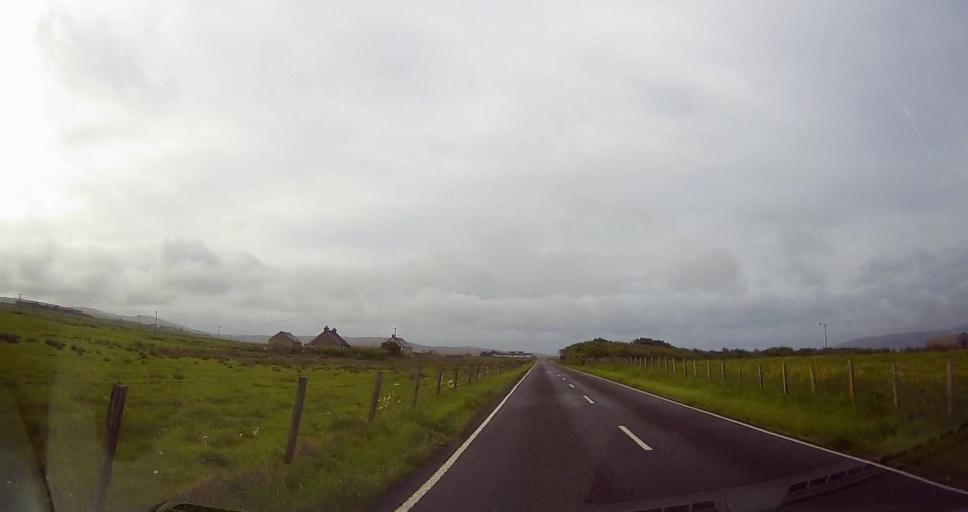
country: GB
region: Scotland
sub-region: Orkney Islands
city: Stromness
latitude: 58.9782
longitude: -3.2427
